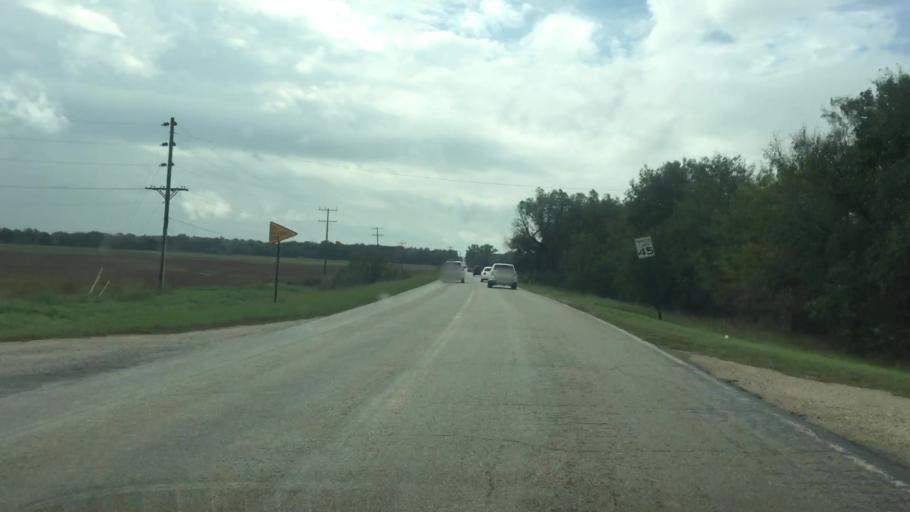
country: US
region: Kansas
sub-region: Allen County
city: Iola
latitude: 37.8783
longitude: -95.4368
